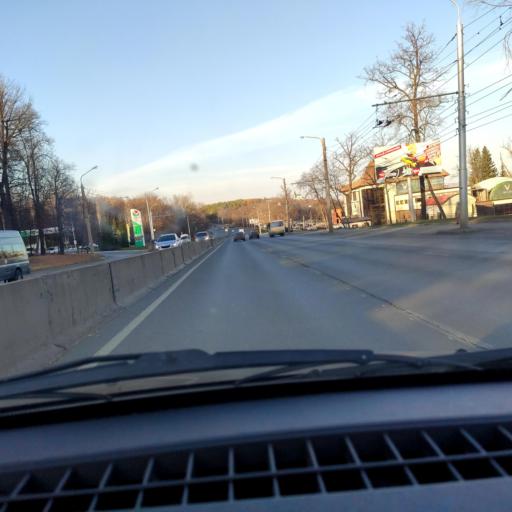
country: RU
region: Bashkortostan
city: Ufa
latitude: 54.7299
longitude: 56.0242
